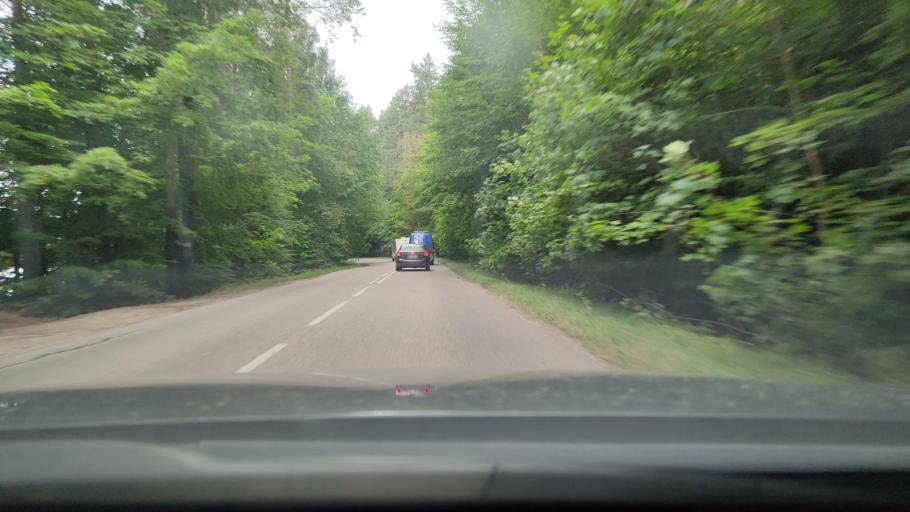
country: PL
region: Pomeranian Voivodeship
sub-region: Powiat pucki
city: Krokowa
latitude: 54.7157
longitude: 18.1661
